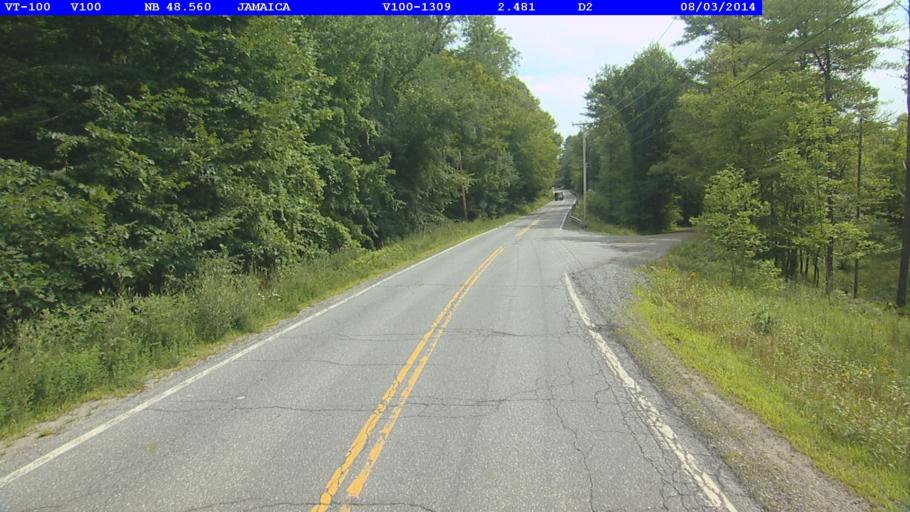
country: US
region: Vermont
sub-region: Windham County
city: Newfane
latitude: 43.0686
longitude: -72.7516
